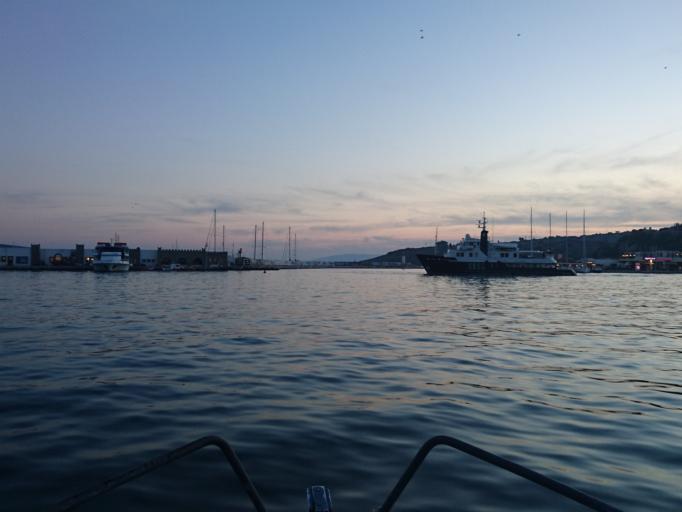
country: TR
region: Mugla
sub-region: Bodrum
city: Bodrum
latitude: 37.0338
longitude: 27.4267
